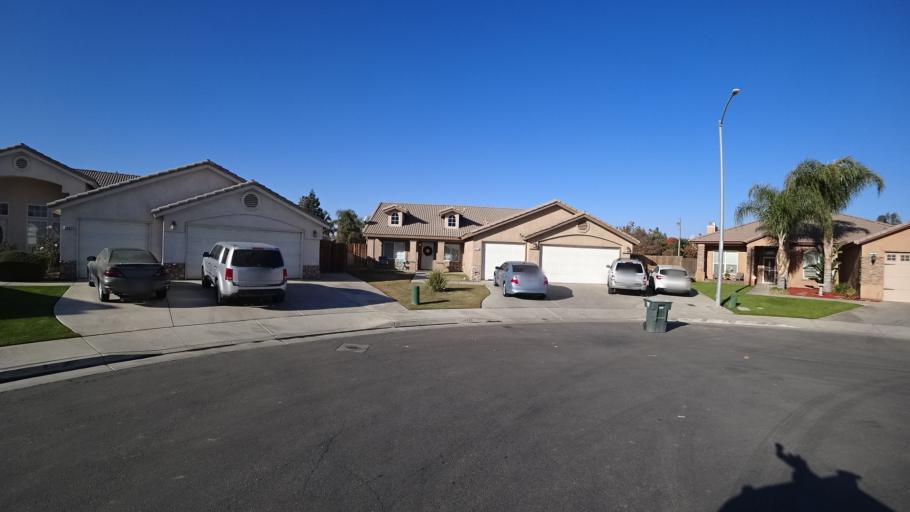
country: US
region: California
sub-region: Kern County
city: Greenfield
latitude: 35.2756
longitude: -119.0383
